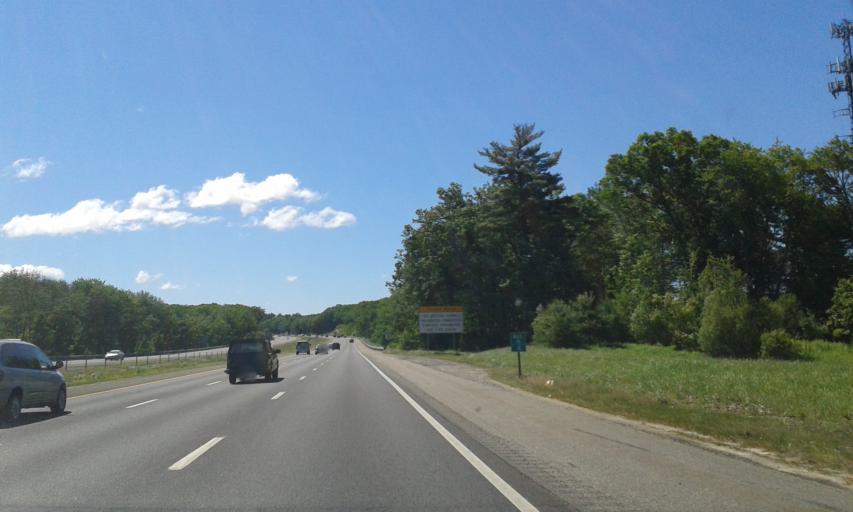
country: US
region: Massachusetts
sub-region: Middlesex County
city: Billerica
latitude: 42.5371
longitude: -71.2800
